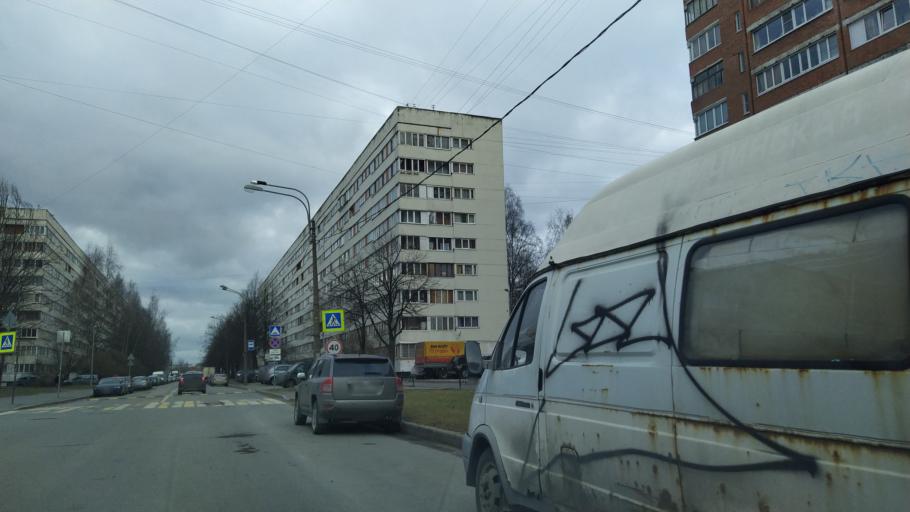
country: RU
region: Leningrad
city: Parnas
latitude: 60.0503
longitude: 30.3697
